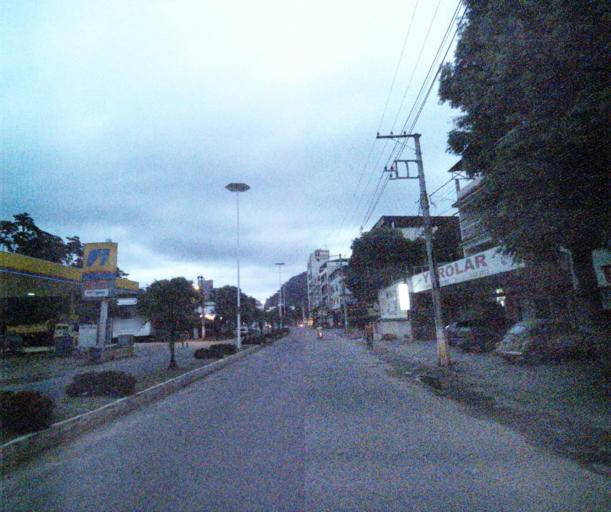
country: BR
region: Espirito Santo
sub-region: Castelo
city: Castelo
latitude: -20.6118
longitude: -41.2048
